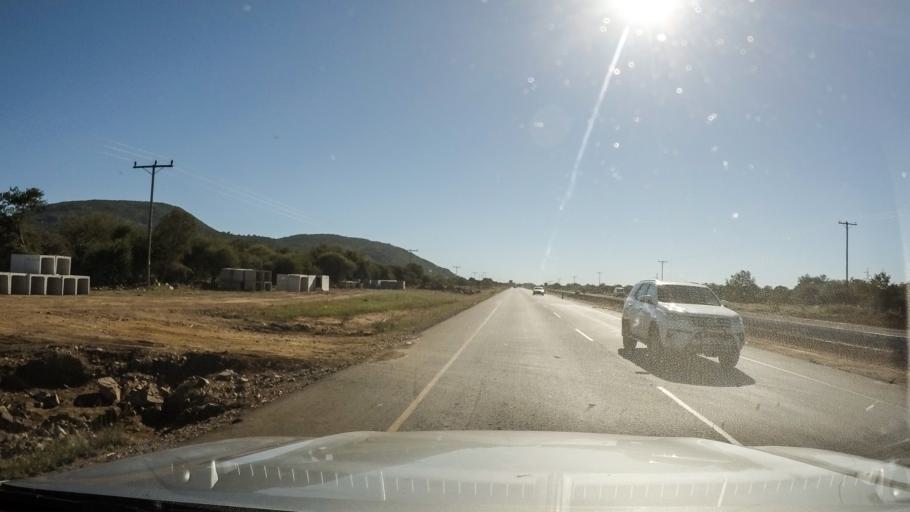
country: BW
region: Kweneng
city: Gabane
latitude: -24.7319
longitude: 25.8461
